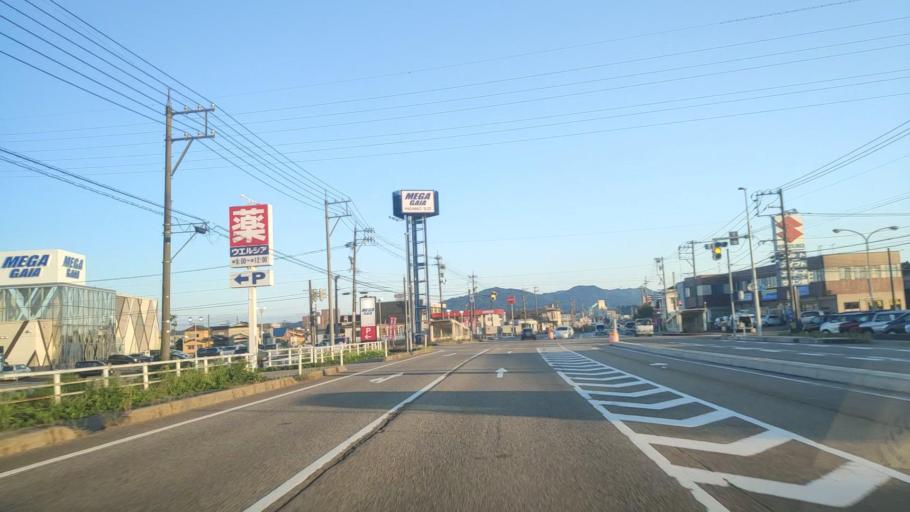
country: JP
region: Toyama
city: Himi
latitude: 36.8357
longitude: 136.9899
